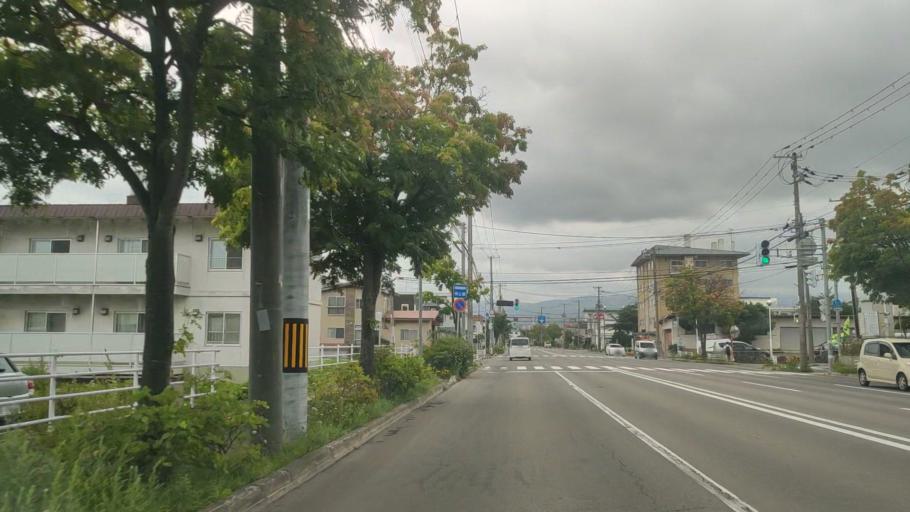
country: JP
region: Hokkaido
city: Hakodate
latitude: 41.7960
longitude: 140.7513
